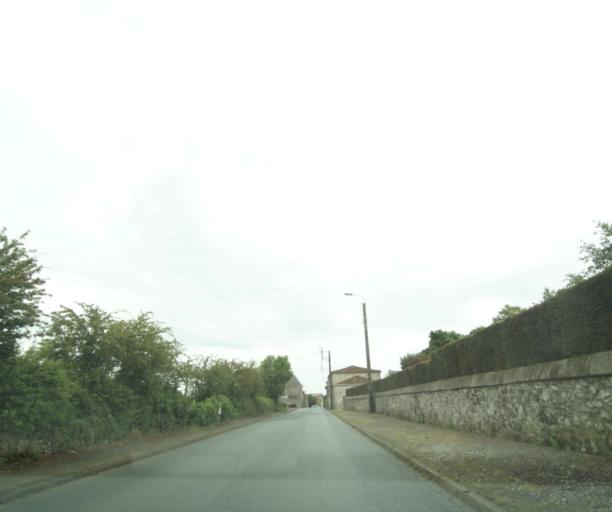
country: FR
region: Poitou-Charentes
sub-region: Departement des Deux-Sevres
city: Viennay
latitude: 46.7316
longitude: -0.2367
